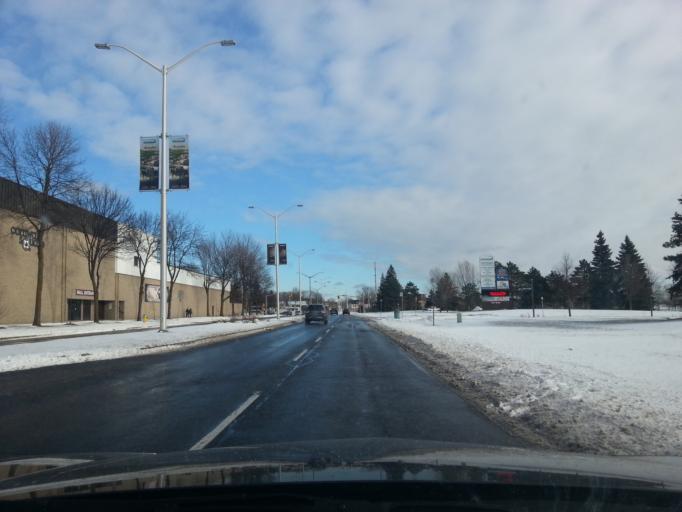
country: CA
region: Ontario
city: Cornwall
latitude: 45.0155
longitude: -74.7257
